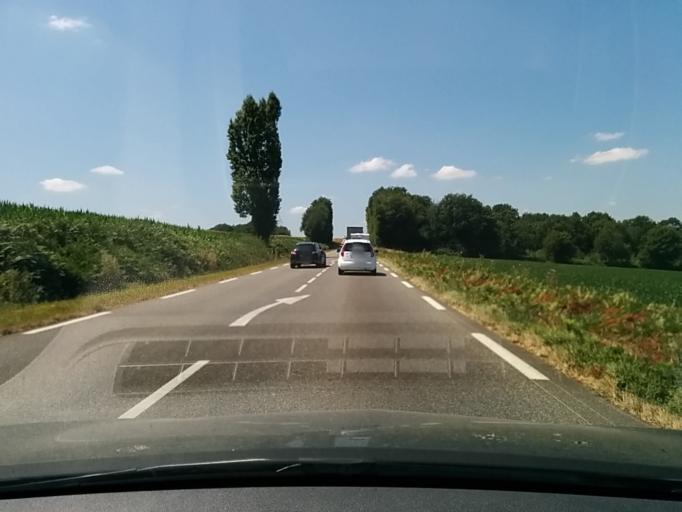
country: FR
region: Midi-Pyrenees
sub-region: Departement du Gers
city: Eauze
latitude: 43.7692
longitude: 0.1460
